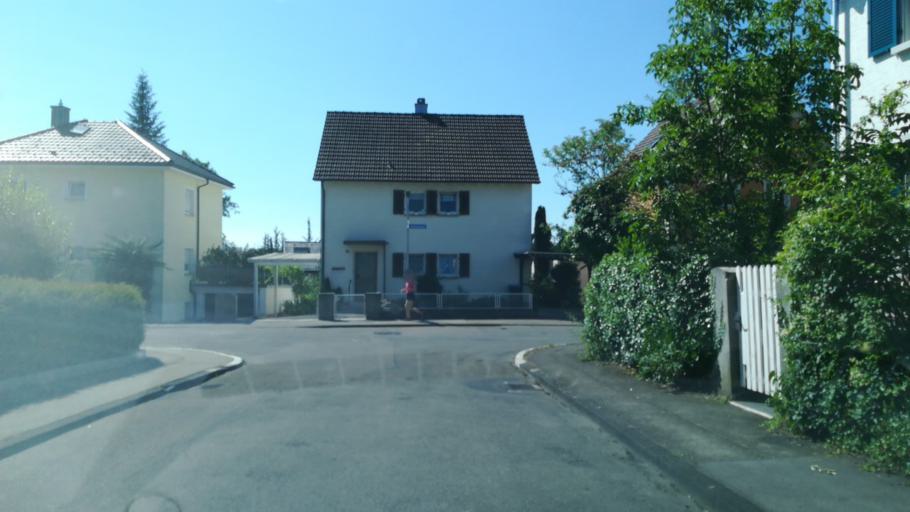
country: DE
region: Baden-Wuerttemberg
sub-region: Freiburg Region
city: Singen
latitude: 47.7673
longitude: 8.8472
